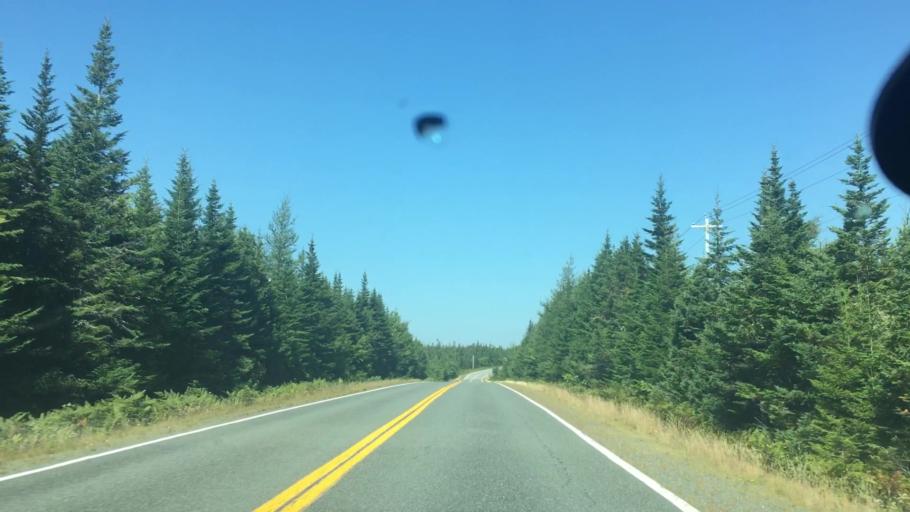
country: CA
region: Nova Scotia
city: Antigonish
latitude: 45.0048
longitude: -62.1032
